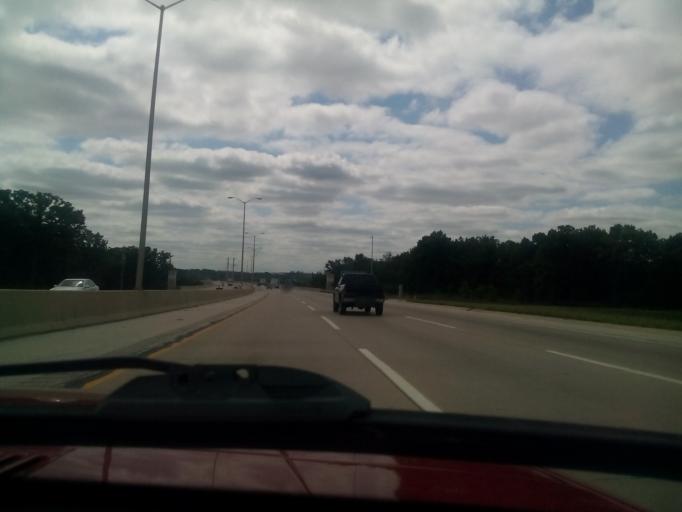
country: US
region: Illinois
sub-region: Cook County
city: Lemont
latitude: 41.6835
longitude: -88.0308
